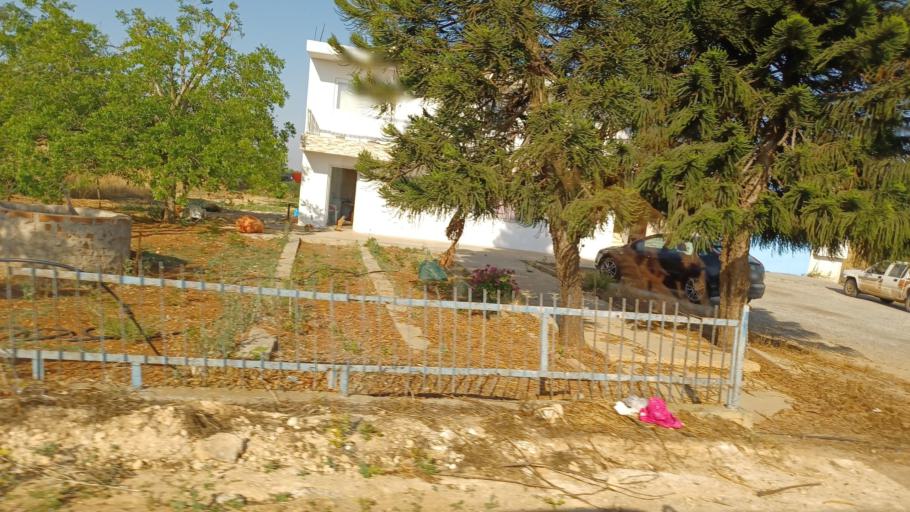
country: CY
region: Ammochostos
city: Frenaros
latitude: 35.0509
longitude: 33.9174
